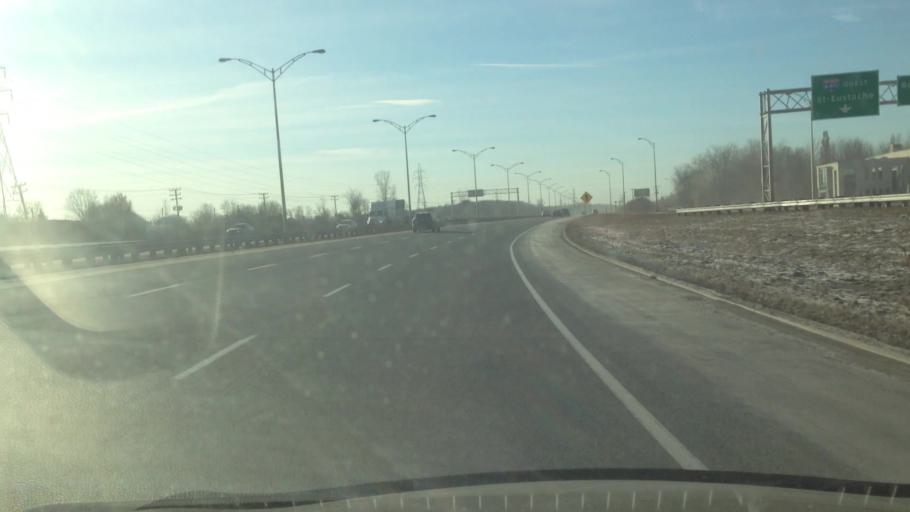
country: CA
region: Quebec
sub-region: Laurentides
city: Boisbriand
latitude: 45.6164
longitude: -73.8503
